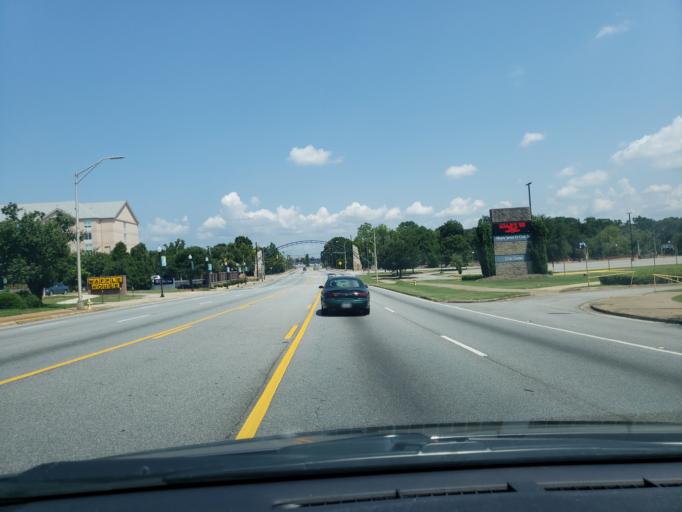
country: US
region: Georgia
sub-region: Dougherty County
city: Albany
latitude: 31.5753
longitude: -84.1508
